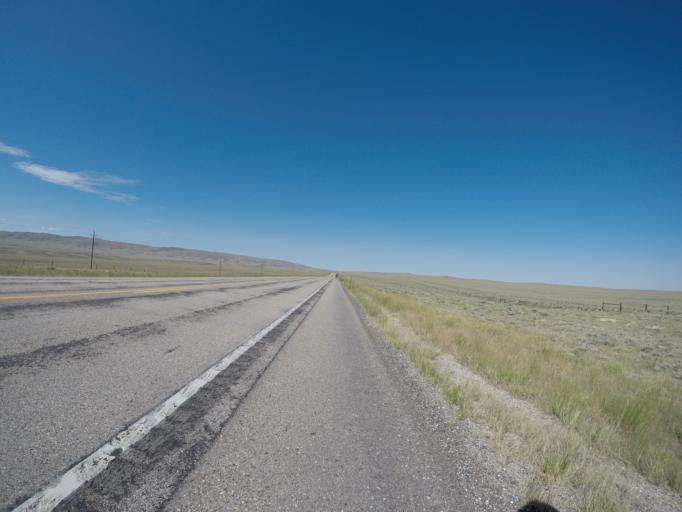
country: US
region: Wyoming
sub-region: Carbon County
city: Saratoga
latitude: 41.8136
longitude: -106.6739
